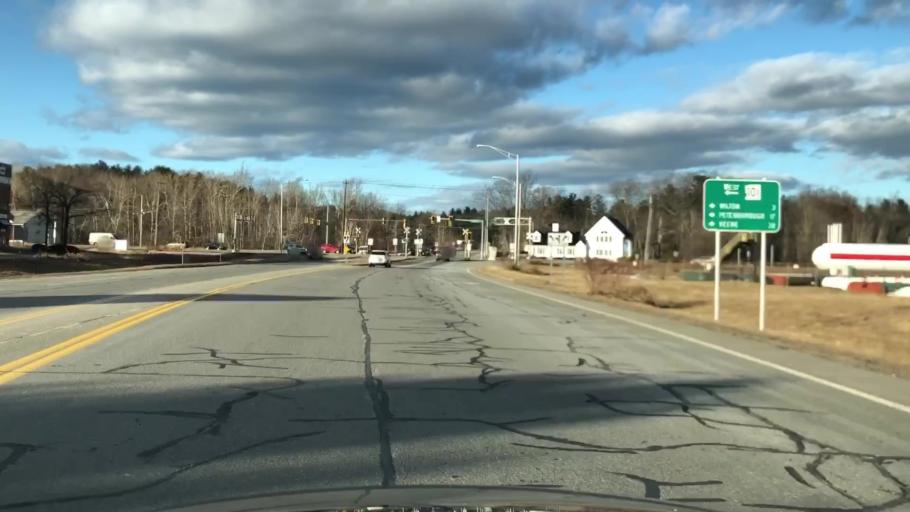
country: US
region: New Hampshire
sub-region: Hillsborough County
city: Wilton
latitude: 42.8409
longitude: -71.7030
